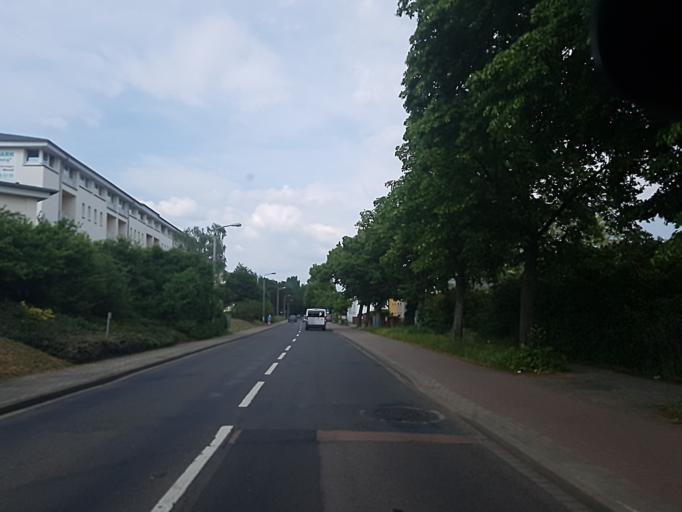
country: DE
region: Saxony-Anhalt
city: Nudersdorf
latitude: 51.8774
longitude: 12.5504
